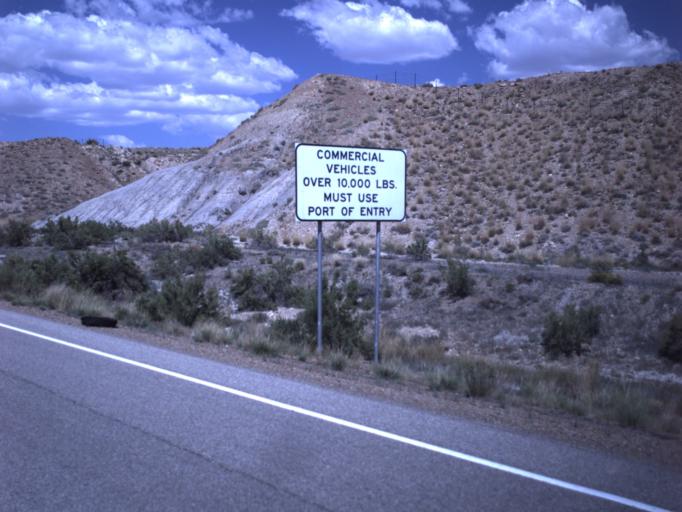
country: US
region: Utah
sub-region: Emery County
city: Huntington
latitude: 39.4435
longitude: -110.8647
